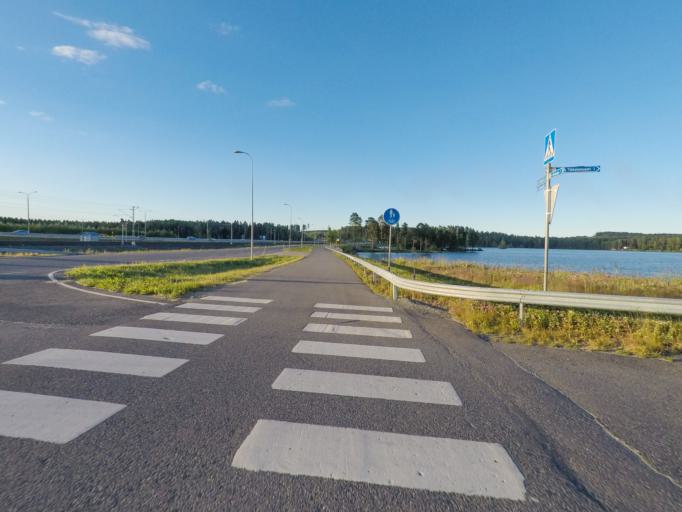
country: FI
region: Northern Savo
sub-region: Kuopio
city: Kuopio
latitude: 62.9505
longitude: 27.6782
